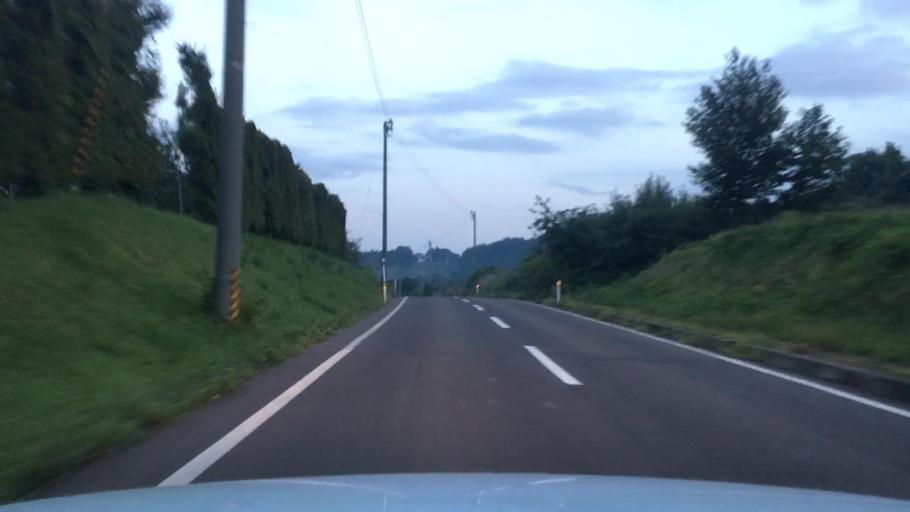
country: JP
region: Aomori
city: Hirosaki
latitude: 40.6736
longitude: 140.3847
